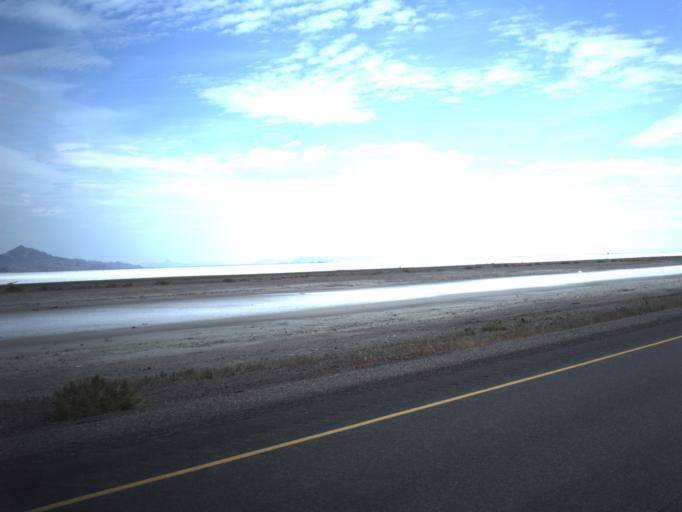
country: US
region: Utah
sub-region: Tooele County
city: Wendover
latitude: 40.7401
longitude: -113.9357
